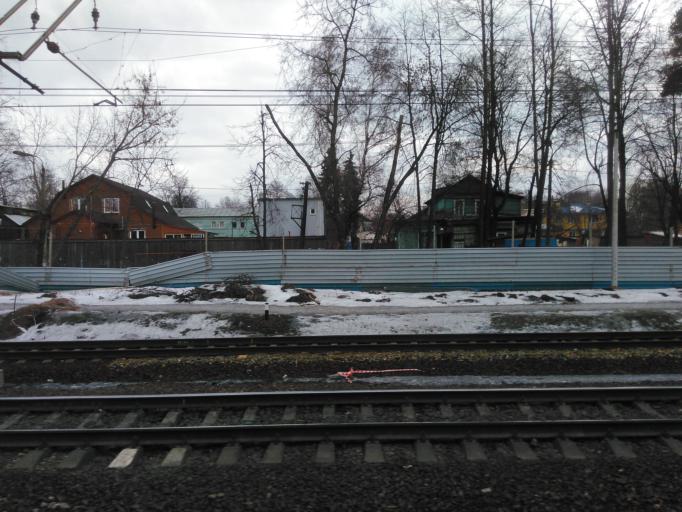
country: RU
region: Moscow
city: Yaroslavskiy
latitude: 55.8915
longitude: 37.7282
